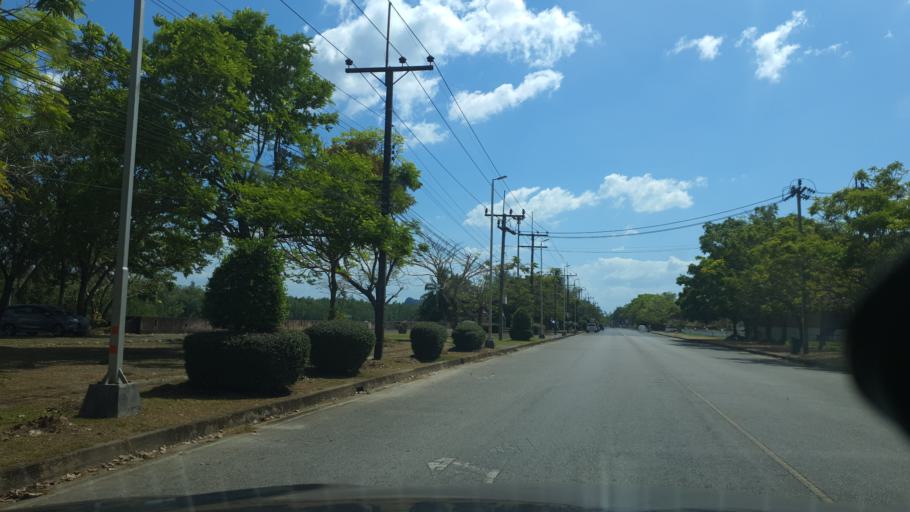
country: TH
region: Phangnga
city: Phang Nga
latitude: 8.4025
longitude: 98.5120
